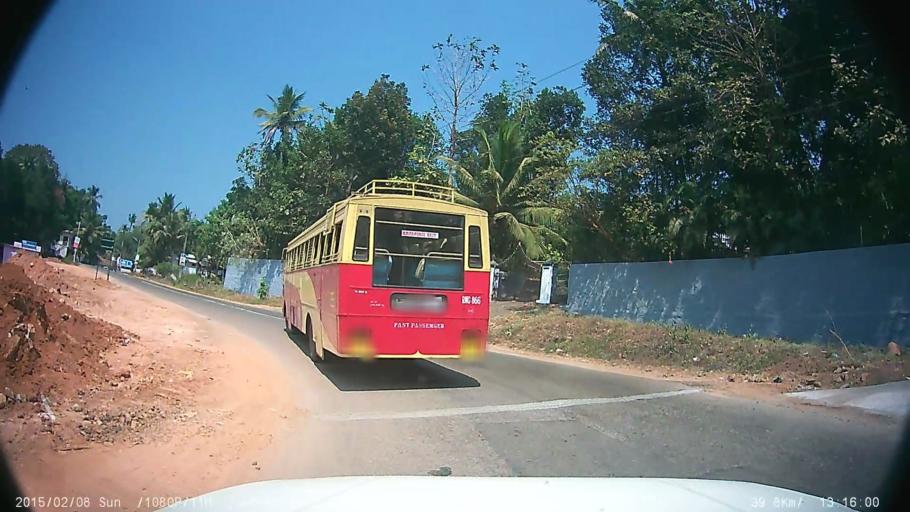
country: IN
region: Kerala
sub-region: Ernakulam
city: Muvattupuzha
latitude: 9.9625
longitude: 76.5790
